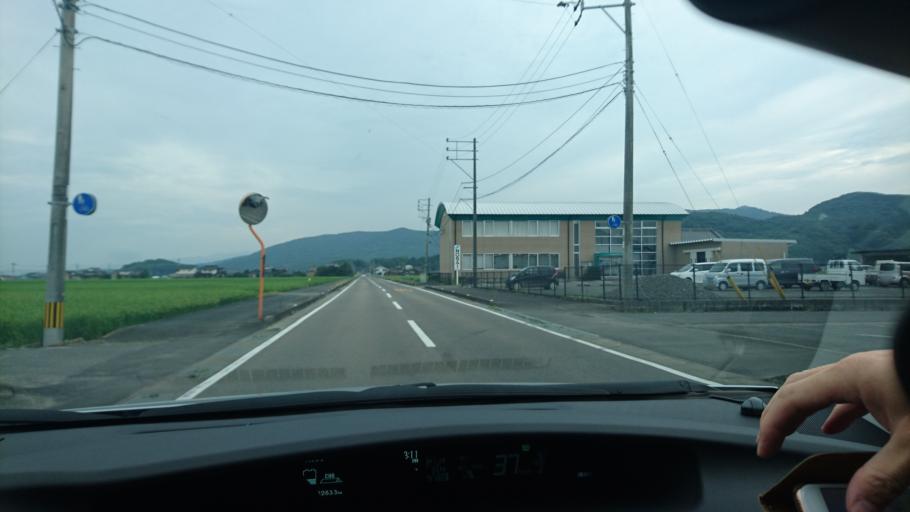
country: JP
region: Saga Prefecture
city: Takeocho-takeo
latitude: 33.1971
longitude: 130.1024
